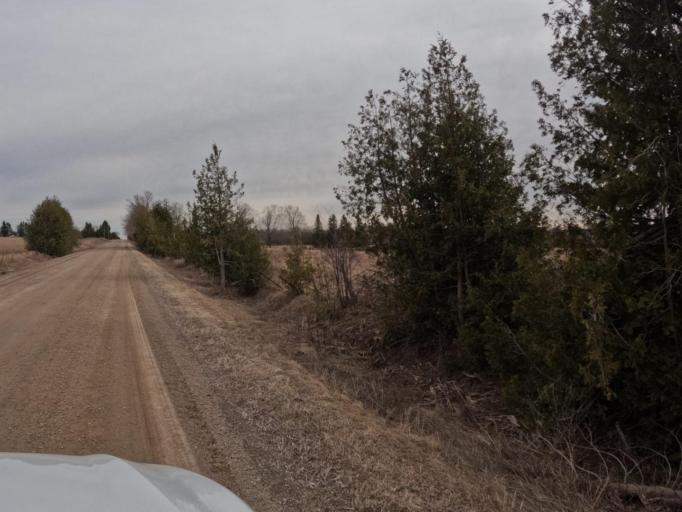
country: CA
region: Ontario
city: Shelburne
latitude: 43.9364
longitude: -80.2591
